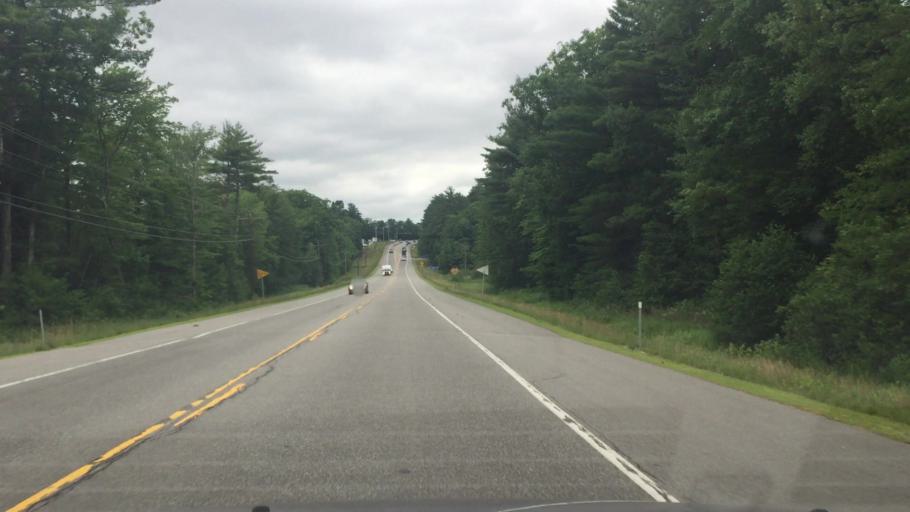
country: US
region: New Hampshire
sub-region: Belknap County
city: Meredith
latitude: 43.6330
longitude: -71.5309
